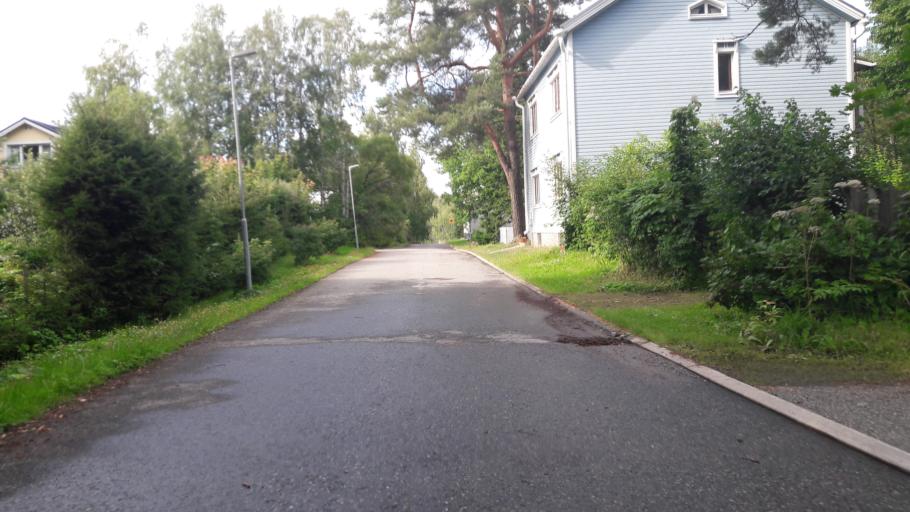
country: FI
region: North Karelia
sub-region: Joensuu
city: Joensuu
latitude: 62.5980
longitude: 29.7902
